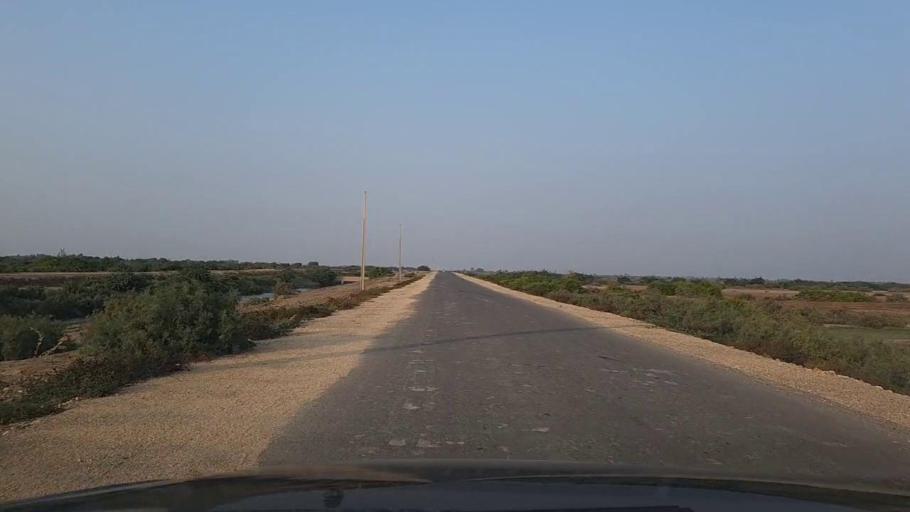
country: PK
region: Sindh
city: Mirpur Sakro
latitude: 24.4652
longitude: 67.7976
